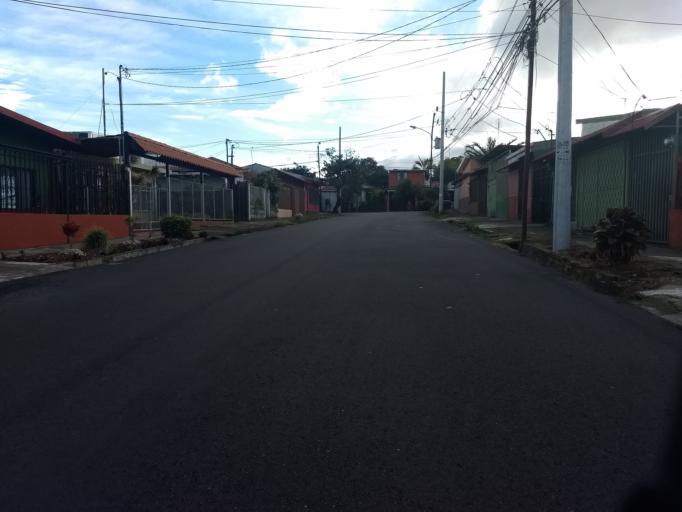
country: CR
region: San Jose
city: San Juan
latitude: 9.9581
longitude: -84.0825
